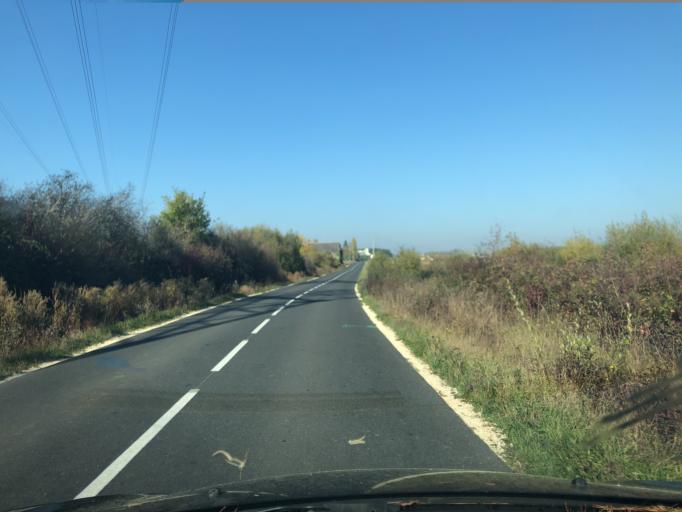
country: FR
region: Centre
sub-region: Departement d'Indre-et-Loire
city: Rouziers-de-Touraine
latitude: 47.4980
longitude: 0.6537
